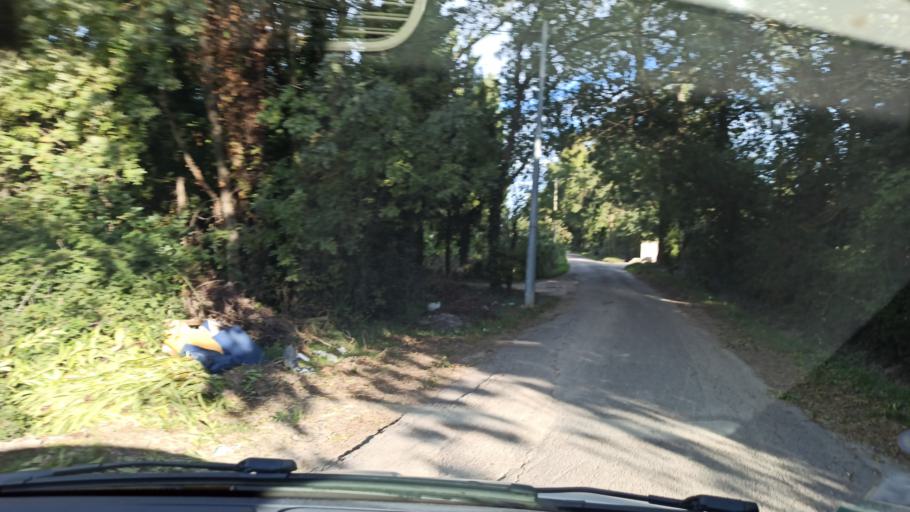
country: FR
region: Provence-Alpes-Cote d'Azur
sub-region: Departement du Vaucluse
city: Montfavet
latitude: 43.9389
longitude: 4.8592
